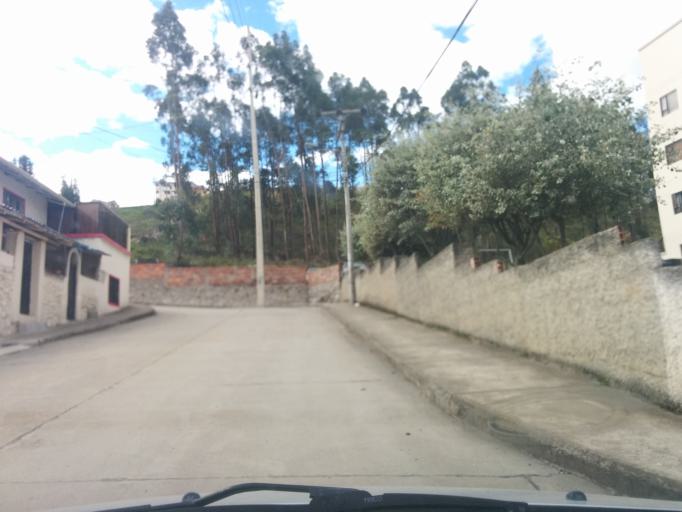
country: EC
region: Azuay
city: Cuenca
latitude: -2.9274
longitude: -79.0473
